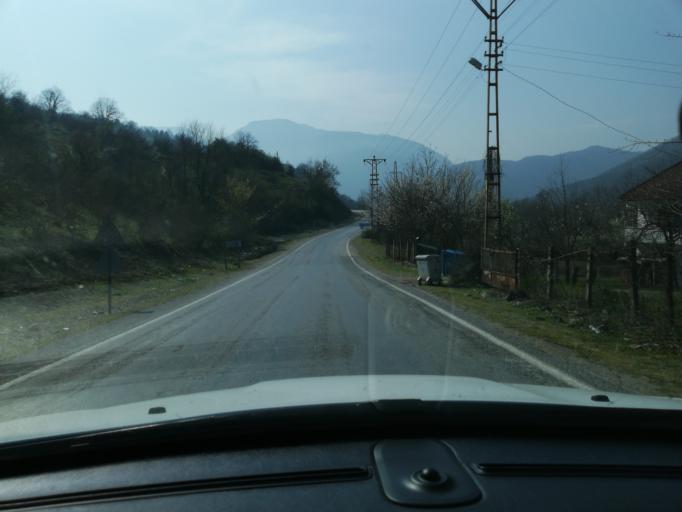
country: TR
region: Karabuk
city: Yenice
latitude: 41.2288
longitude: 32.3610
